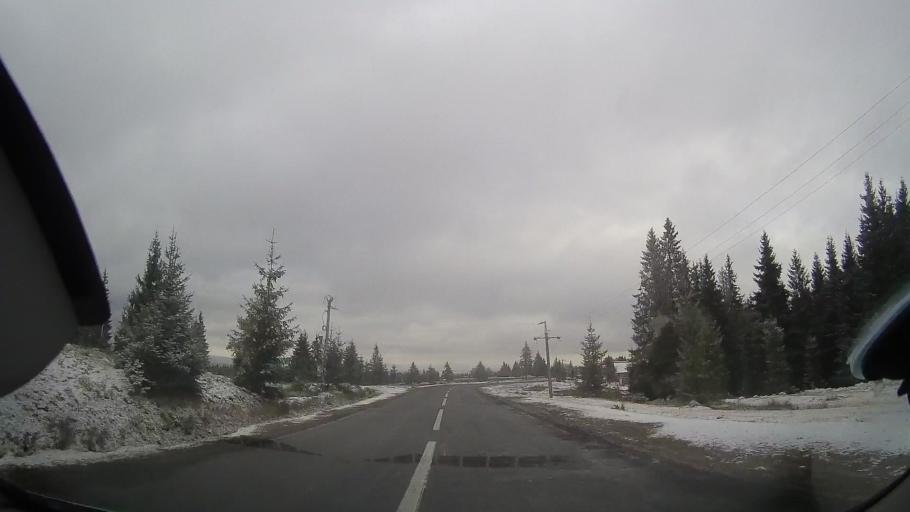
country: RO
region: Cluj
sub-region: Comuna Belis
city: Belis
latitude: 46.7005
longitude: 23.0363
